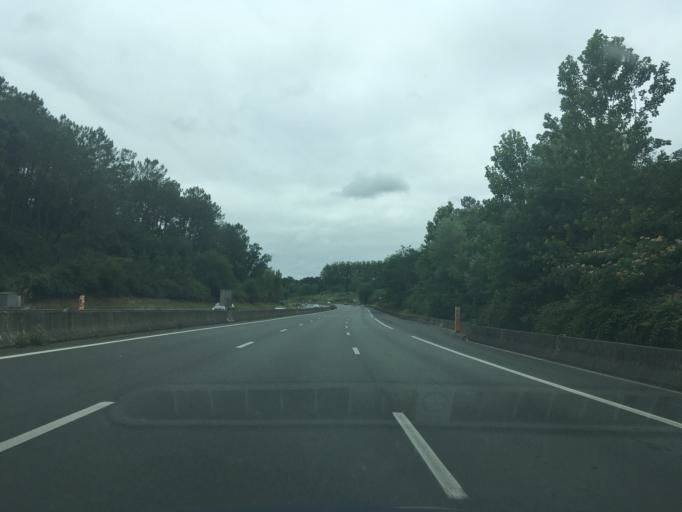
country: FR
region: Aquitaine
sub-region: Departement des Pyrenees-Atlantiques
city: Boucau
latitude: 43.5167
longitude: -1.4427
